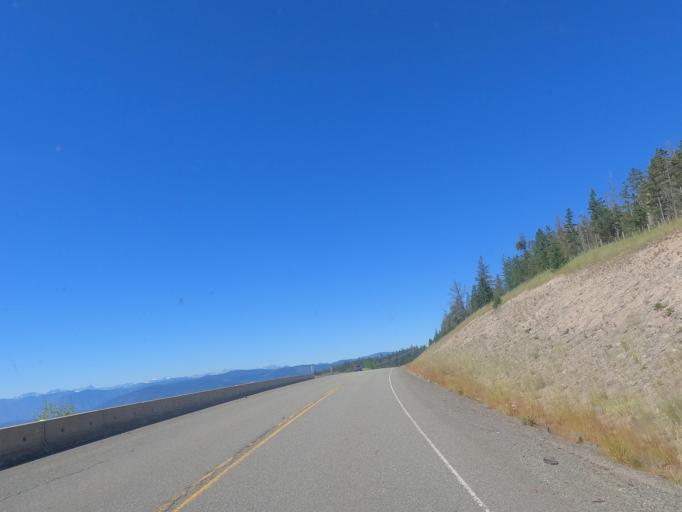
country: CA
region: British Columbia
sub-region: Thompson-Nicola Regional District
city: Ashcroft
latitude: 50.5704
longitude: -121.1811
